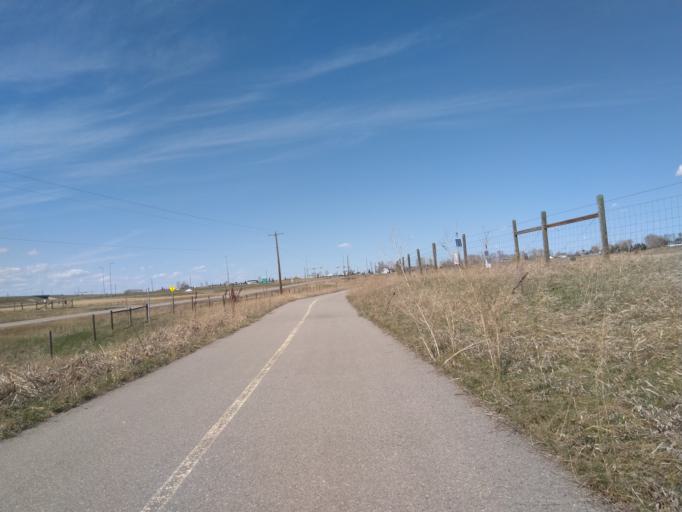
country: CA
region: Alberta
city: Chestermere
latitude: 50.9449
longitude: -113.9114
